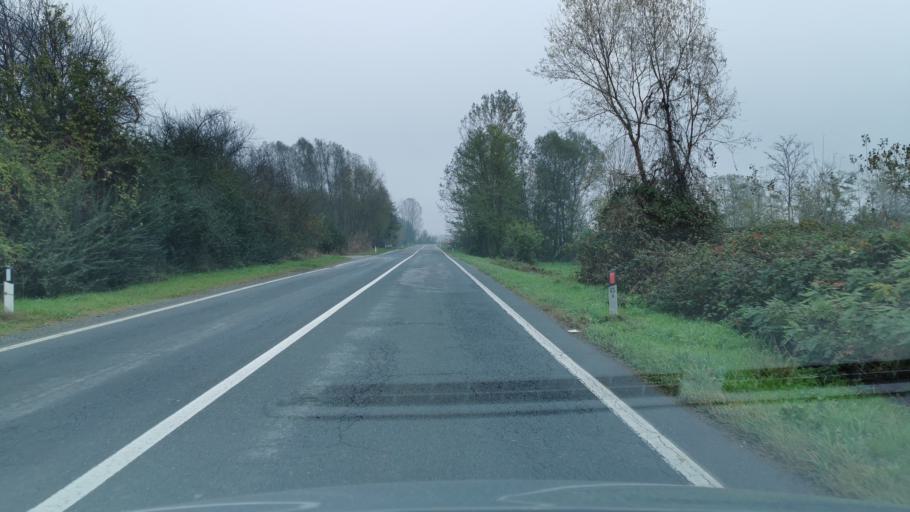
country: IT
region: Piedmont
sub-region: Provincia di Torino
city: Strambino
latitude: 45.3871
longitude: 7.9027
